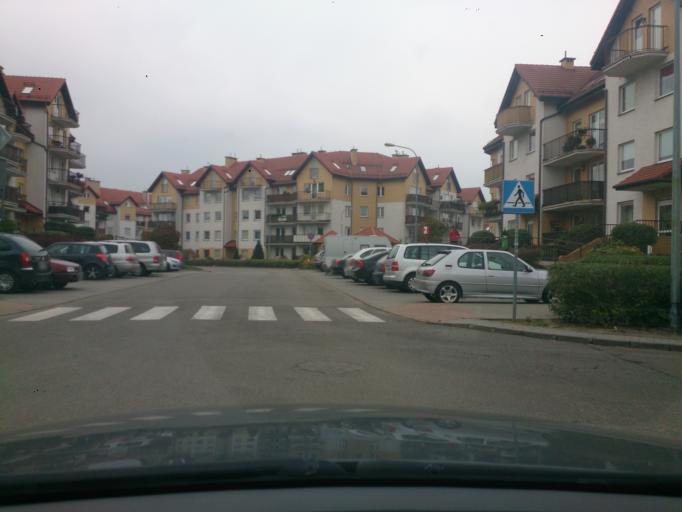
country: PL
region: Pomeranian Voivodeship
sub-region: Gdynia
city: Wielki Kack
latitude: 54.4655
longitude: 18.4838
